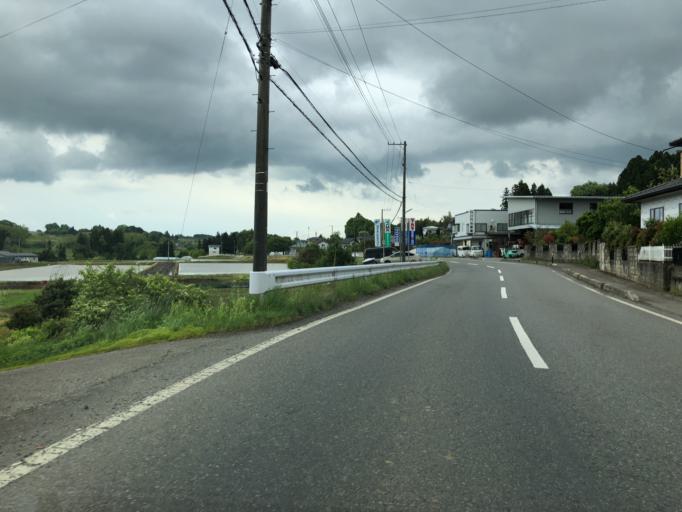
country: JP
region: Fukushima
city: Ishikawa
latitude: 37.1815
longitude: 140.4056
